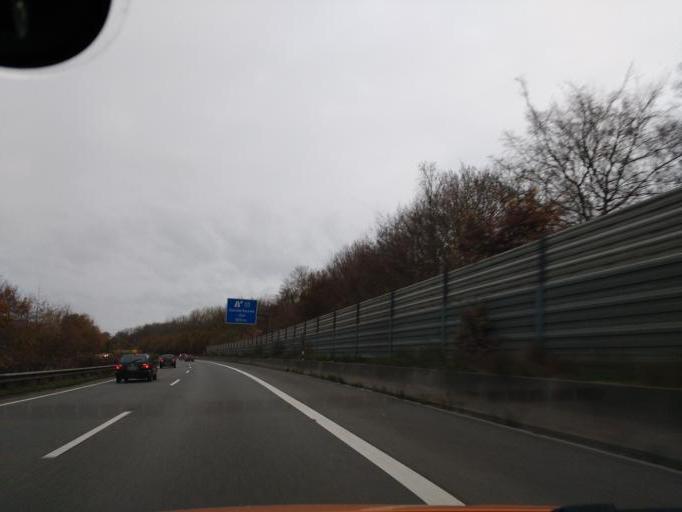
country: DE
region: Lower Saxony
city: Ganderkesee
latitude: 53.0441
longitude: 8.5791
